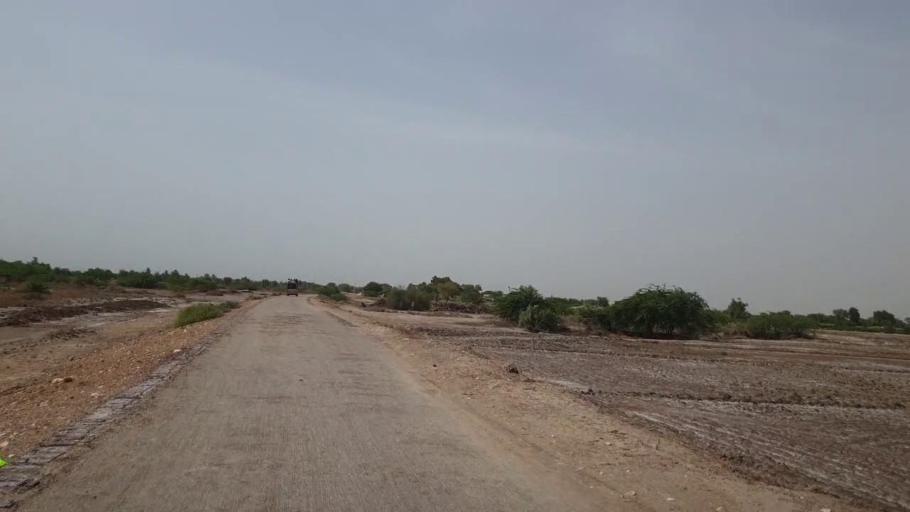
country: PK
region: Sindh
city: Bandhi
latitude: 26.5654
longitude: 68.3808
